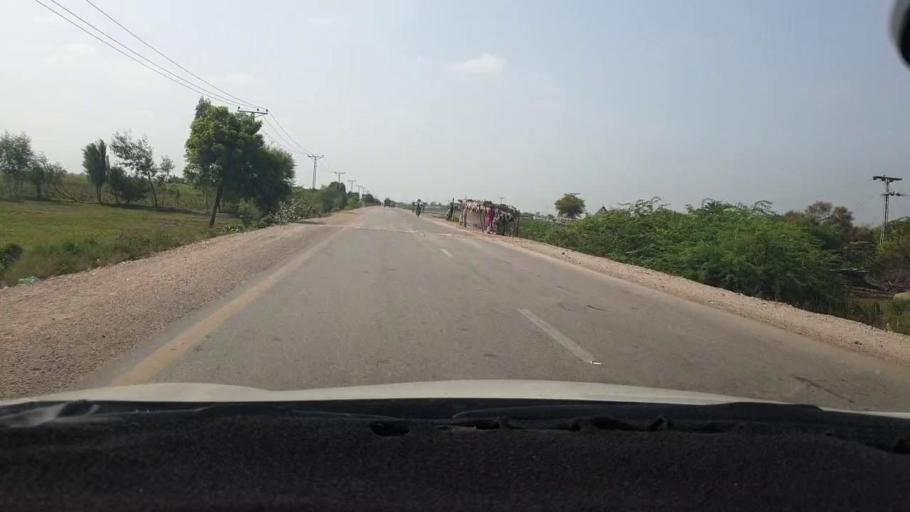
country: PK
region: Sindh
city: Tando Mittha Khan
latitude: 25.7846
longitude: 69.0713
